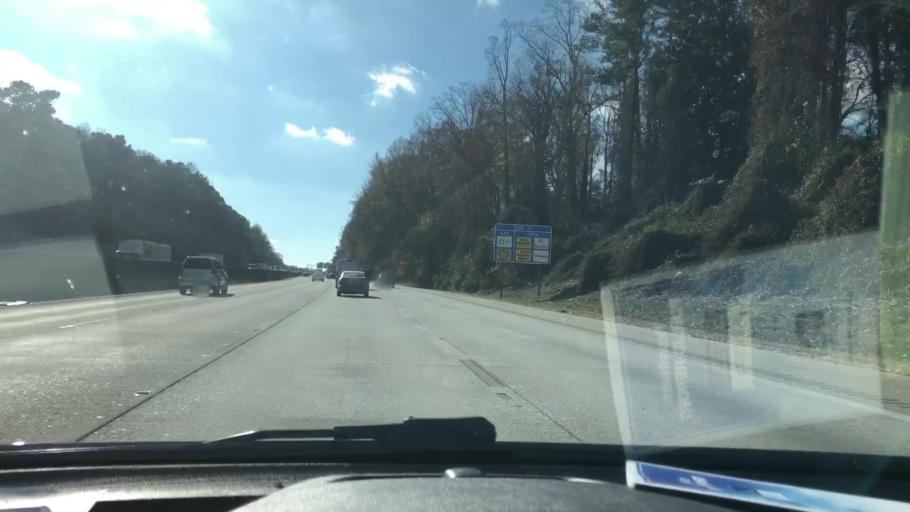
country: US
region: Georgia
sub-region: DeKalb County
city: Tucker
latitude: 33.8674
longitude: -84.2487
